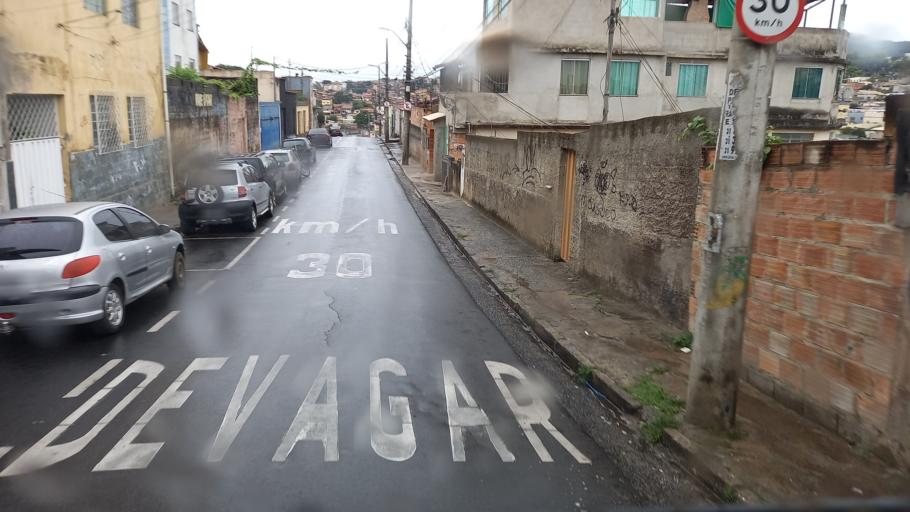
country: BR
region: Minas Gerais
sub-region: Belo Horizonte
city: Belo Horizonte
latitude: -19.9143
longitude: -43.9043
